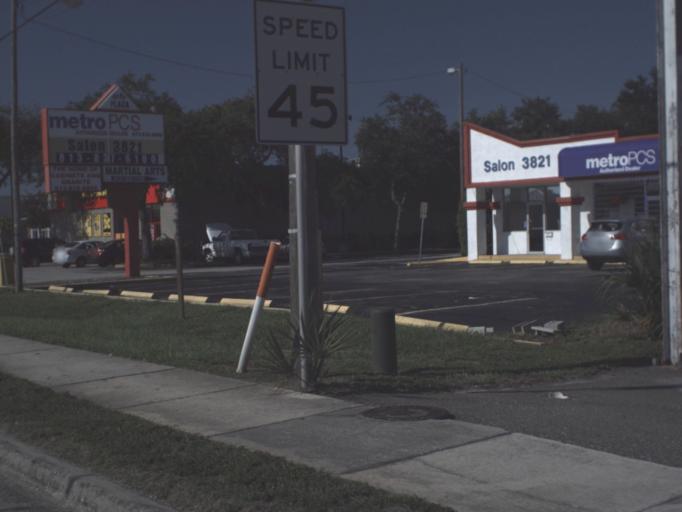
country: US
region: Florida
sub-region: Hillsborough County
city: Tampa
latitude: 27.9081
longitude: -82.5062
